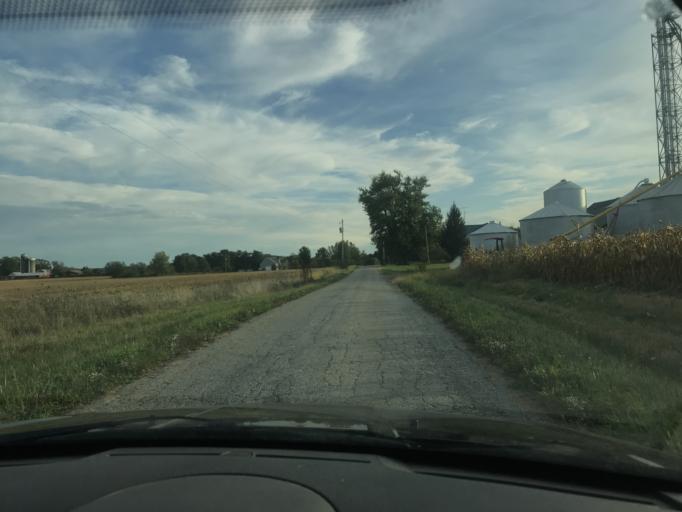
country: US
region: Ohio
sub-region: Logan County
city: West Liberty
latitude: 40.2009
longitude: -83.8071
